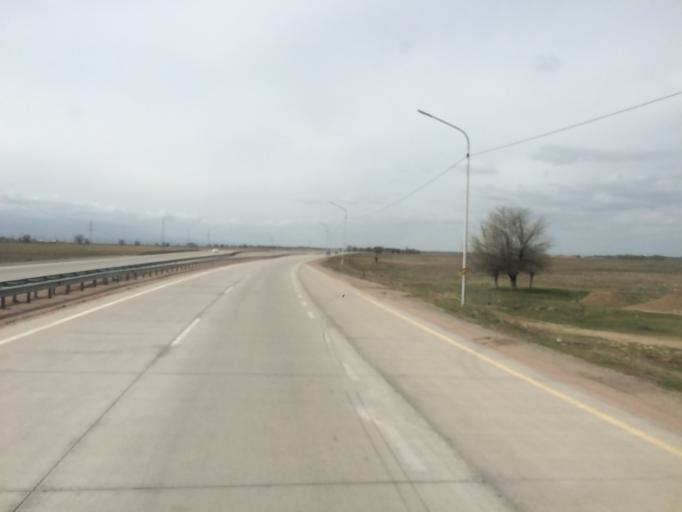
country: KG
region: Talas
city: Ivanovo-Alekseyevka
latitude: 42.9939
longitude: 72.0856
